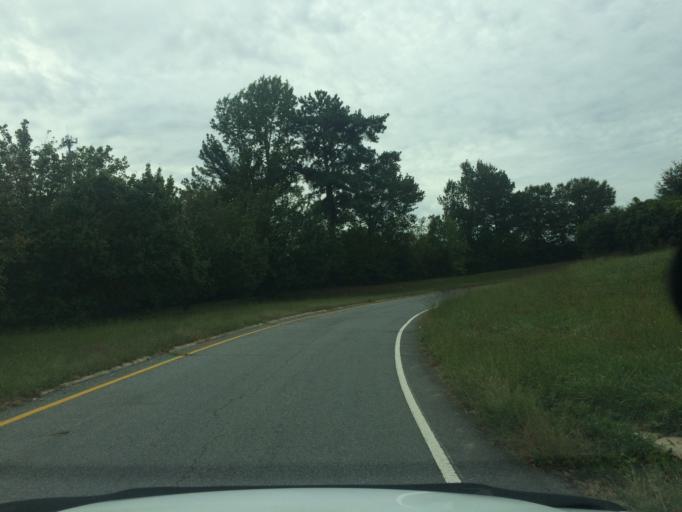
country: US
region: Georgia
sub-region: Cobb County
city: Smyrna
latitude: 33.9224
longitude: -84.5030
